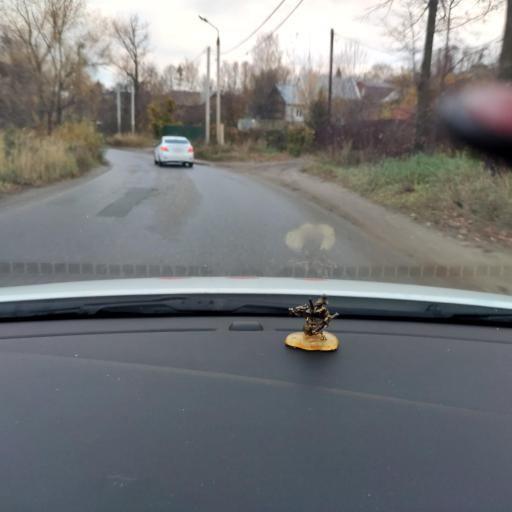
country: RU
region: Tatarstan
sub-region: Gorod Kazan'
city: Kazan
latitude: 55.7261
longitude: 49.1579
